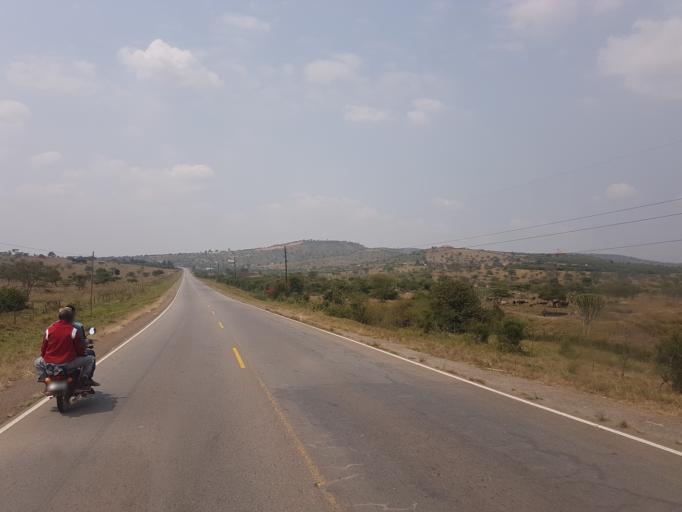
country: UG
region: Western Region
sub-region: Mbarara District
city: Mbarara
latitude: -0.5084
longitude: 30.8410
